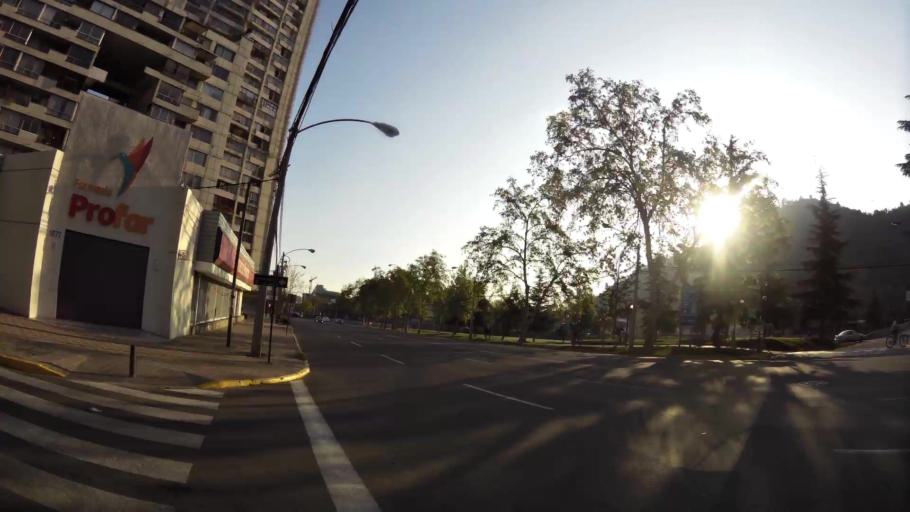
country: CL
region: Santiago Metropolitan
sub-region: Provincia de Santiago
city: Santiago
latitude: -33.4289
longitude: -70.6230
